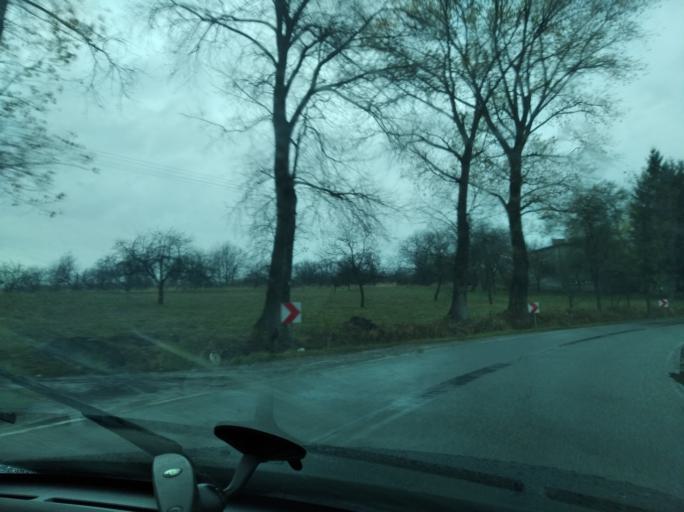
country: PL
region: Subcarpathian Voivodeship
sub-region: Powiat lancucki
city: Albigowa
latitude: 50.0090
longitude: 22.2159
